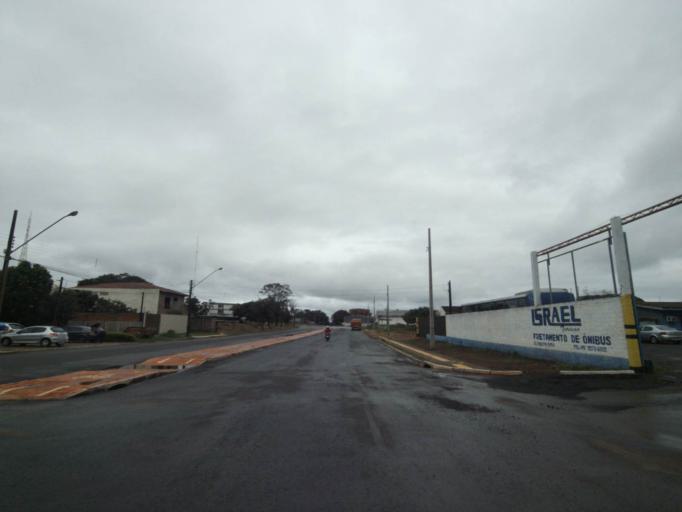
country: BR
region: Parana
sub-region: Foz Do Iguacu
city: Foz do Iguacu
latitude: -25.5152
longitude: -54.5612
